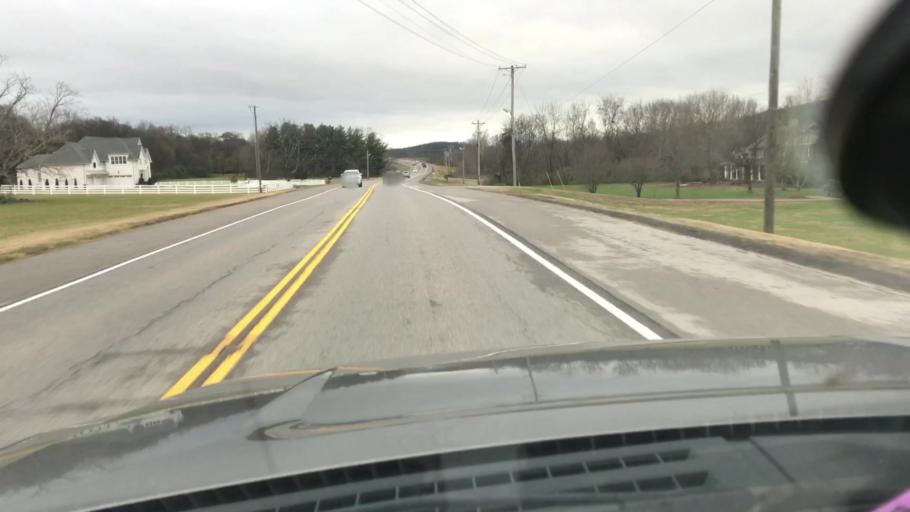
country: US
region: Tennessee
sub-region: Williamson County
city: Brentwood Estates
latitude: 35.9662
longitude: -86.7726
